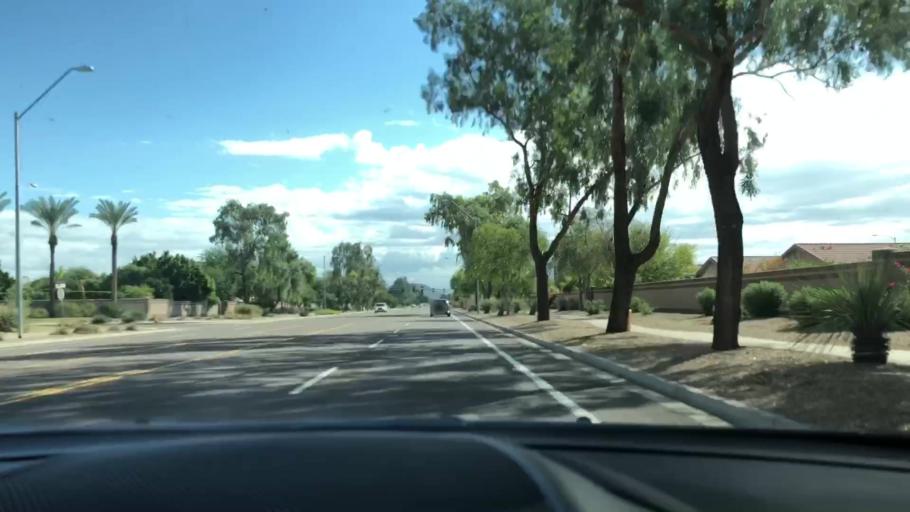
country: US
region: Arizona
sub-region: Maricopa County
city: Sun City
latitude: 33.6816
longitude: -112.2320
